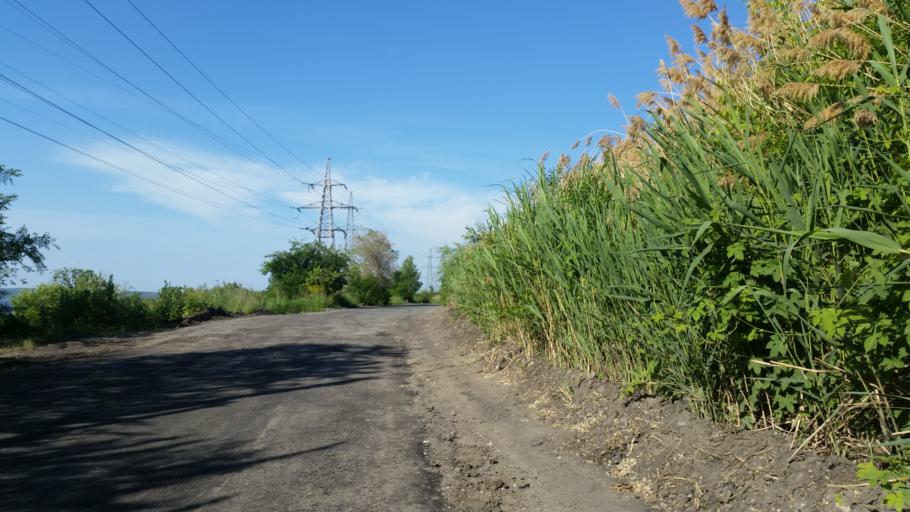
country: RU
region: Ulyanovsk
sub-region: Ulyanovskiy Rayon
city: Ulyanovsk
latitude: 54.3068
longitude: 48.4073
